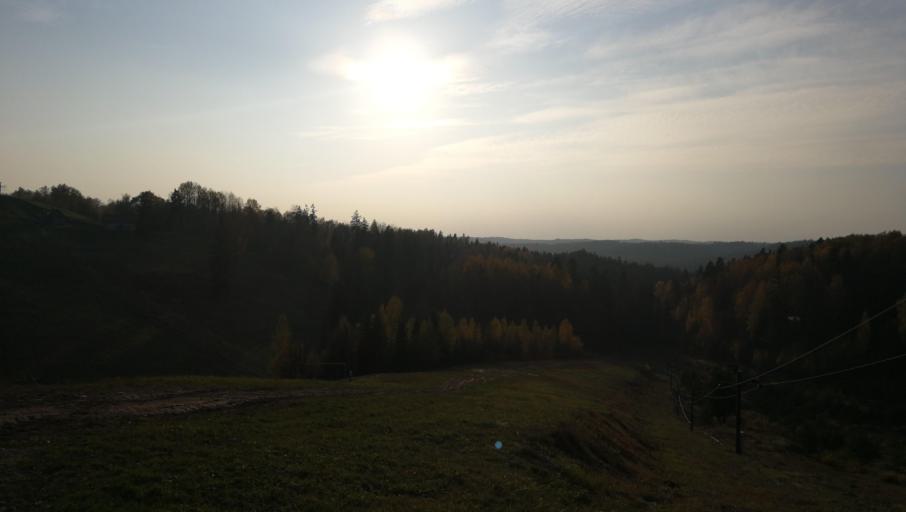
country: LV
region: Cesu Rajons
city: Cesis
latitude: 57.3007
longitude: 25.2299
